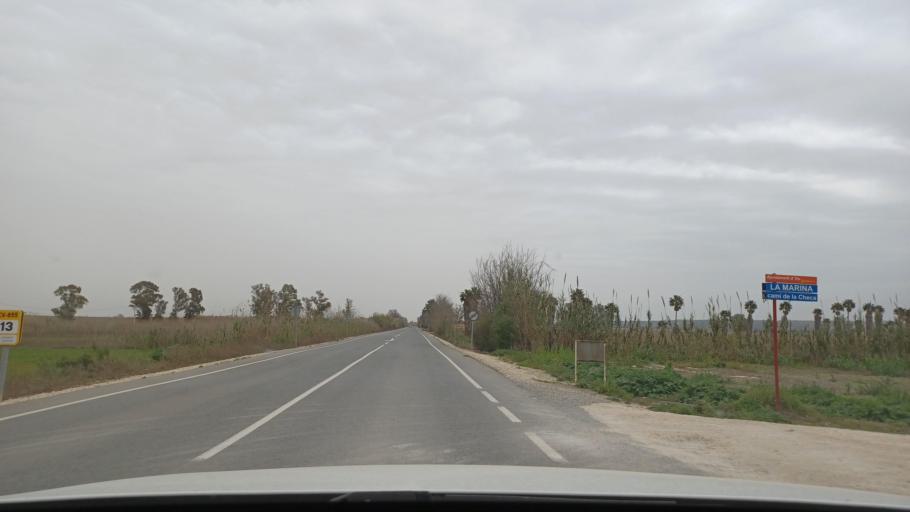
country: ES
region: Valencia
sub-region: Provincia de Alicante
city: Daya Vieja
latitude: 38.1454
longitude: -0.7279
